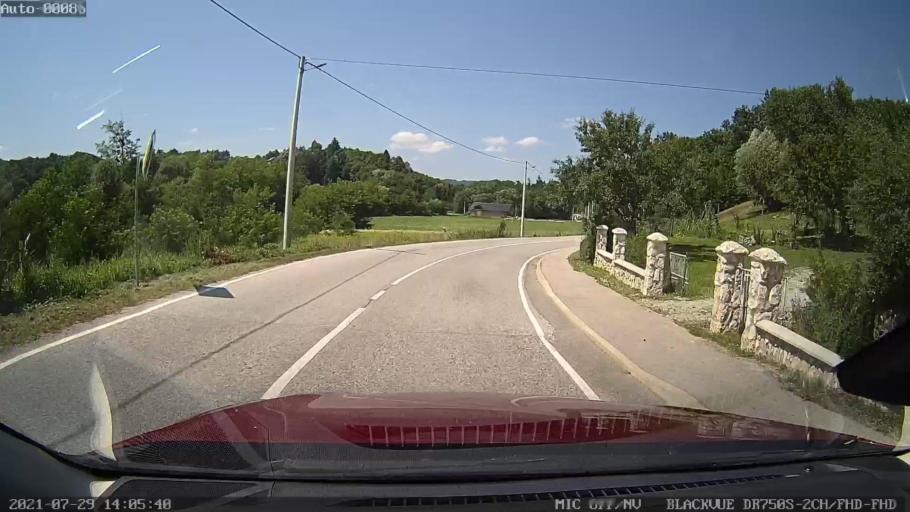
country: HR
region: Varazdinska
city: Lepoglava
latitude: 46.2515
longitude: 15.9576
